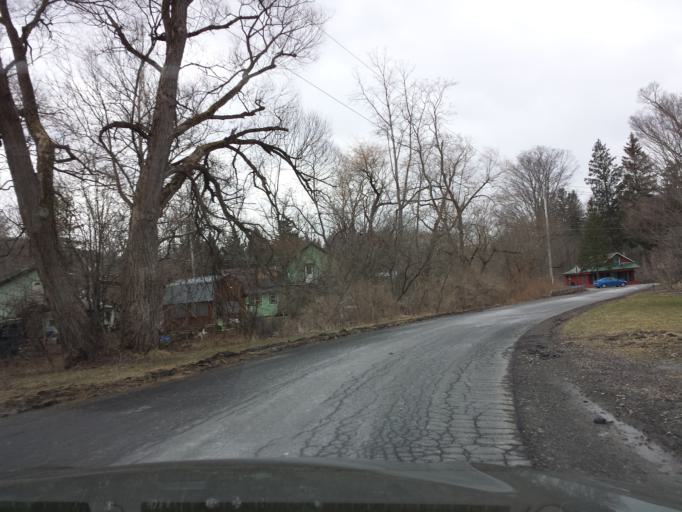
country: US
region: New York
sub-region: Tompkins County
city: Dryden
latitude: 42.3937
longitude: -76.3425
